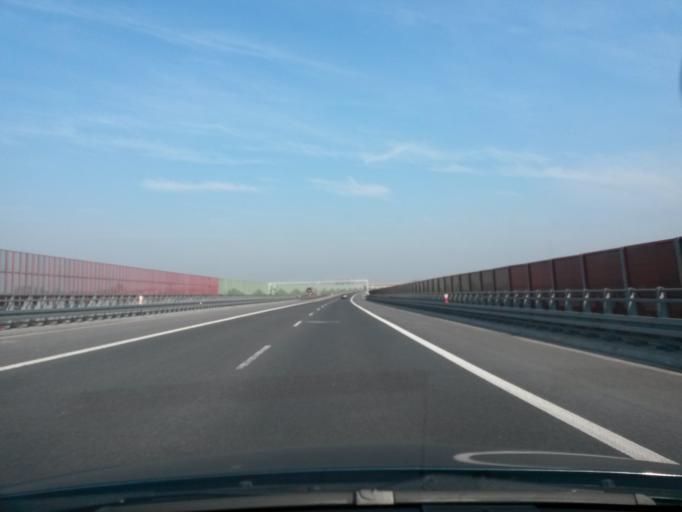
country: PL
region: Lodz Voivodeship
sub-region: Powiat kutnowski
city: Krzyzanow
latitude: 52.1408
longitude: 19.4834
